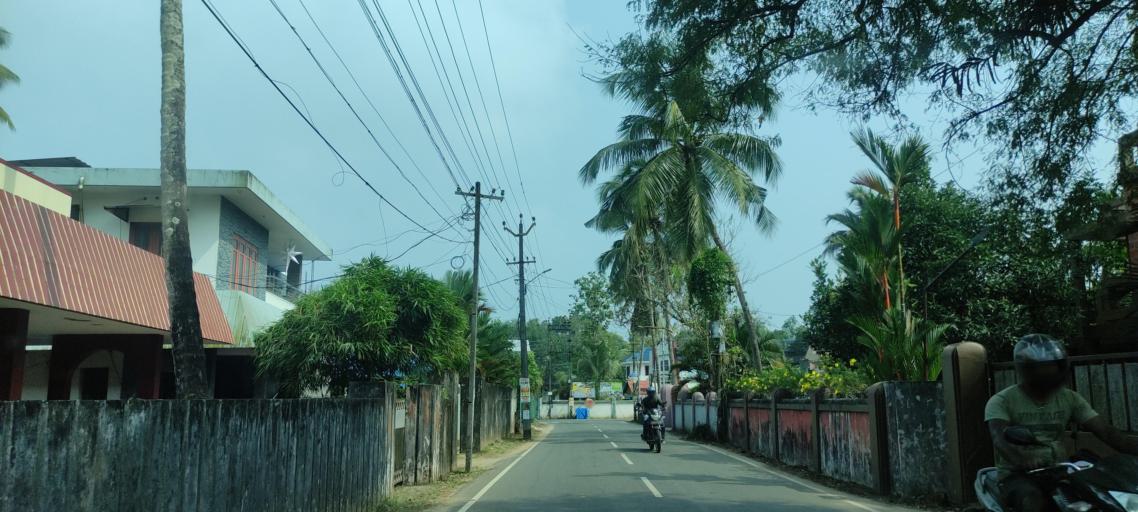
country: IN
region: Kerala
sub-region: Alappuzha
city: Vayalar
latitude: 9.6842
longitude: 76.3355
